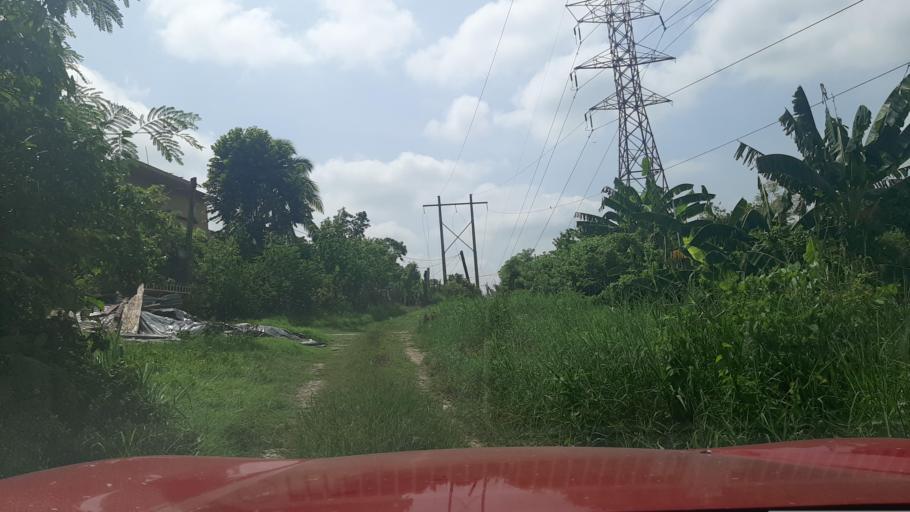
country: MX
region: Veracruz
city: Coatzintla
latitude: 20.4802
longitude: -97.4694
